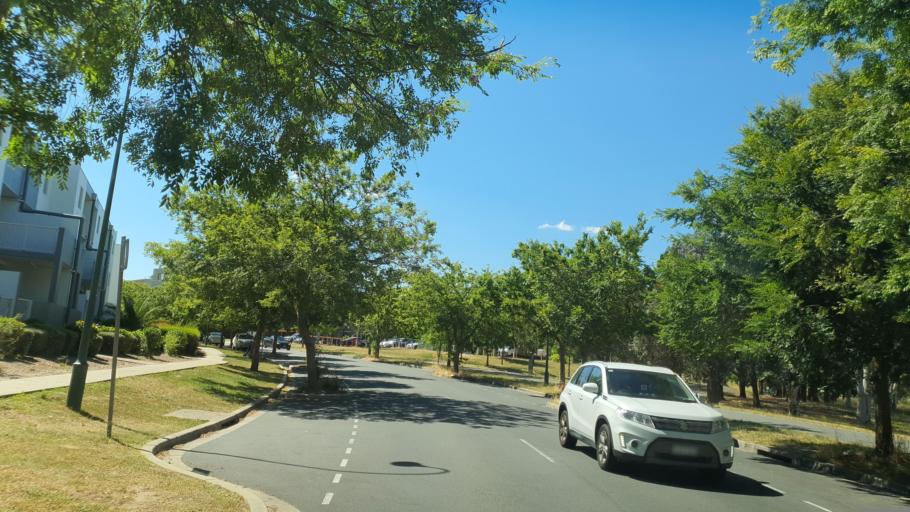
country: AU
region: Australian Capital Territory
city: Macquarie
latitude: -35.2347
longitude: 149.0654
